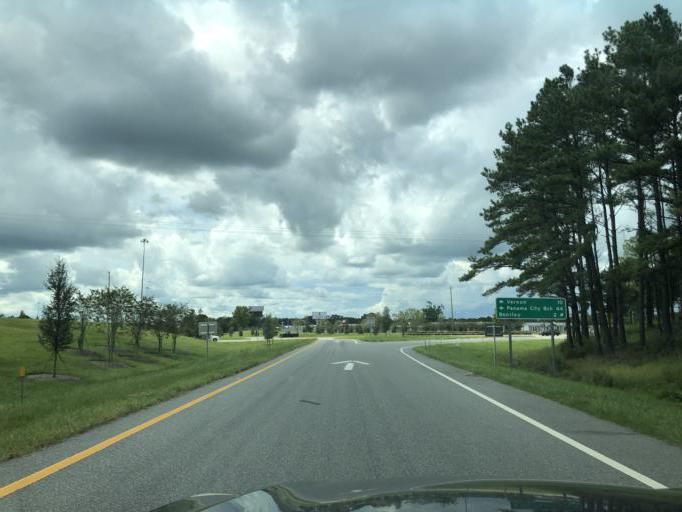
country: US
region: Florida
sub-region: Holmes County
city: Bonifay
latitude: 30.7634
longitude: -85.6834
